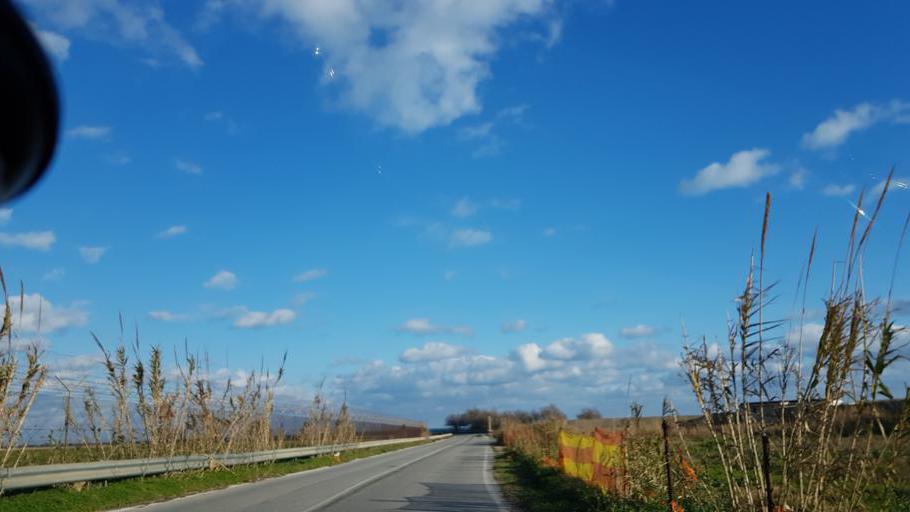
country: IT
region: Apulia
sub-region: Provincia di Brindisi
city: Materdomini
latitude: 40.6611
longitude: 17.9570
